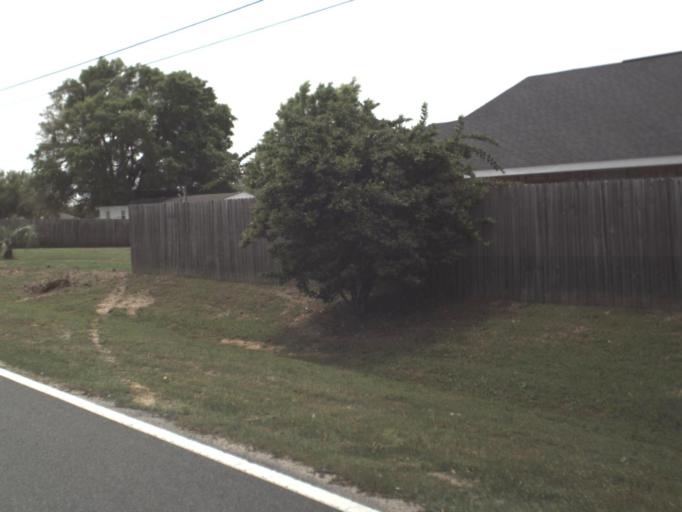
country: US
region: Florida
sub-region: Escambia County
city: Bellview
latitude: 30.4794
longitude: -87.3236
